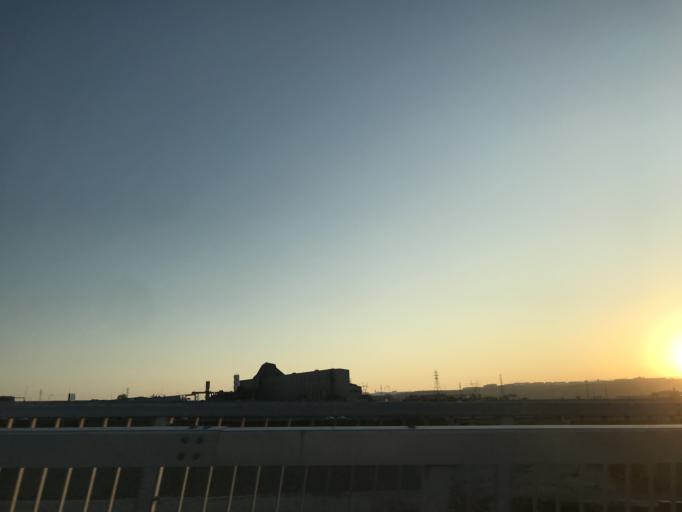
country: TR
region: Kocaeli
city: Tavsanli
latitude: 40.7950
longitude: 29.5066
